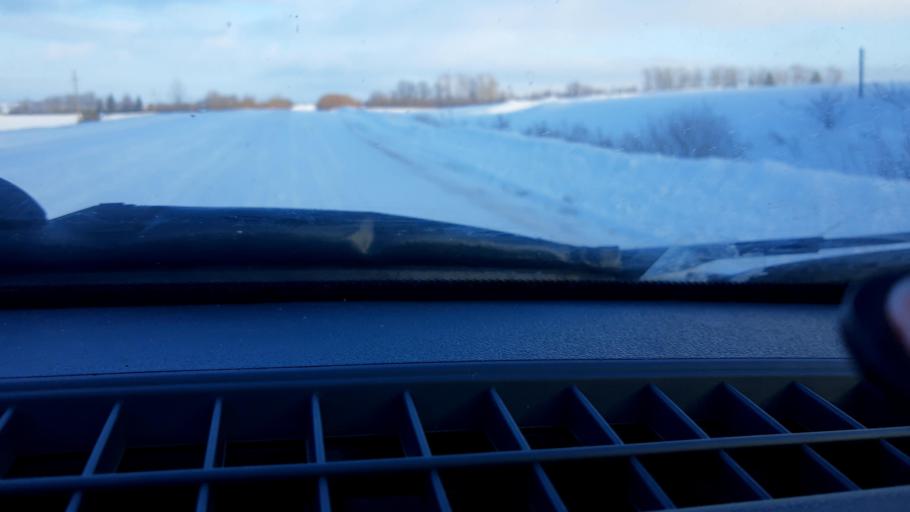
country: RU
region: Bashkortostan
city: Kushnarenkovo
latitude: 55.1232
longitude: 55.5928
